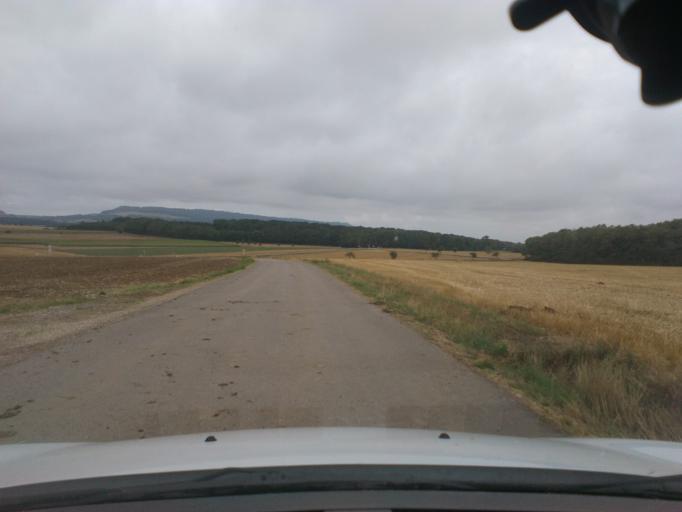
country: FR
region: Lorraine
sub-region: Departement des Vosges
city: Mirecourt
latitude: 48.3637
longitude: 6.1255
